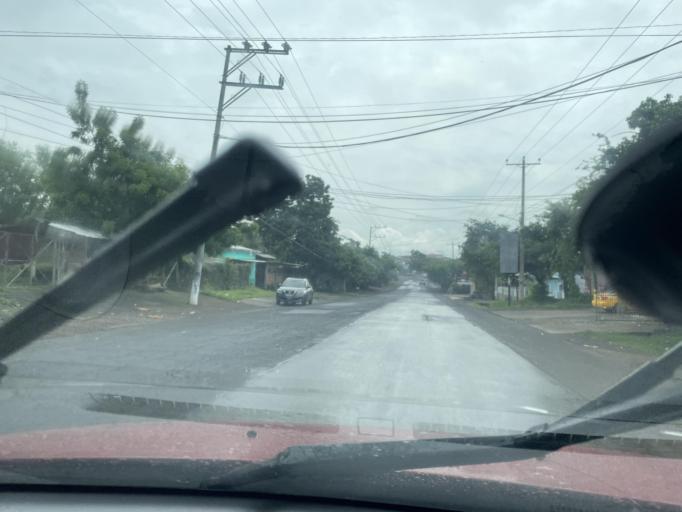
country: SV
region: La Union
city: Santa Rosa de Lima
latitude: 13.6167
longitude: -87.9025
